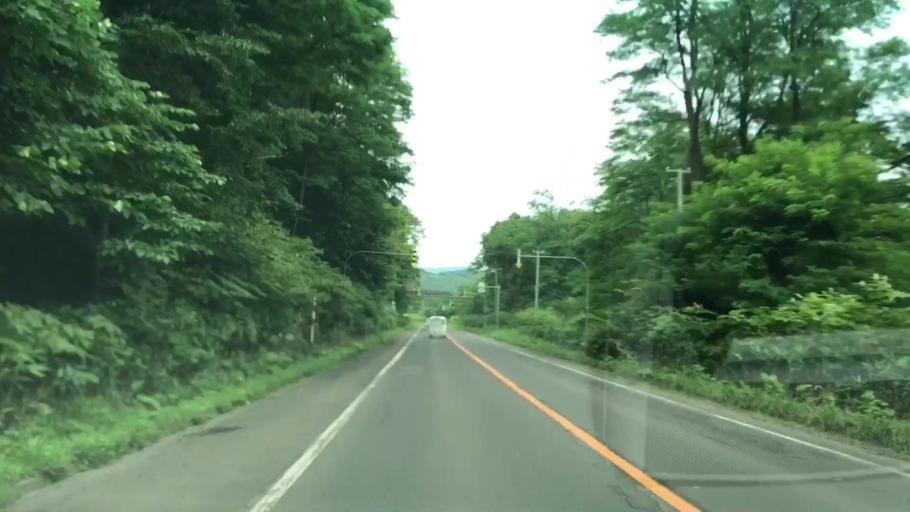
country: JP
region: Hokkaido
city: Niseko Town
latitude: 42.9534
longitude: 140.6972
